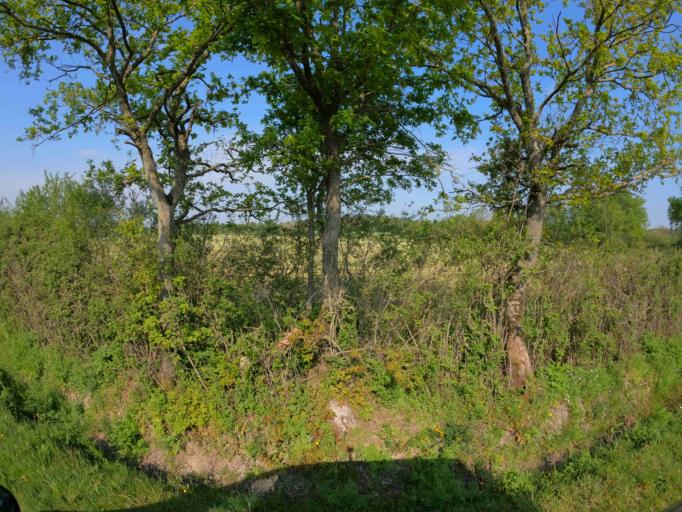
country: FR
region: Pays de la Loire
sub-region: Departement de la Vendee
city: Treize-Septiers
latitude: 47.0025
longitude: -1.2268
